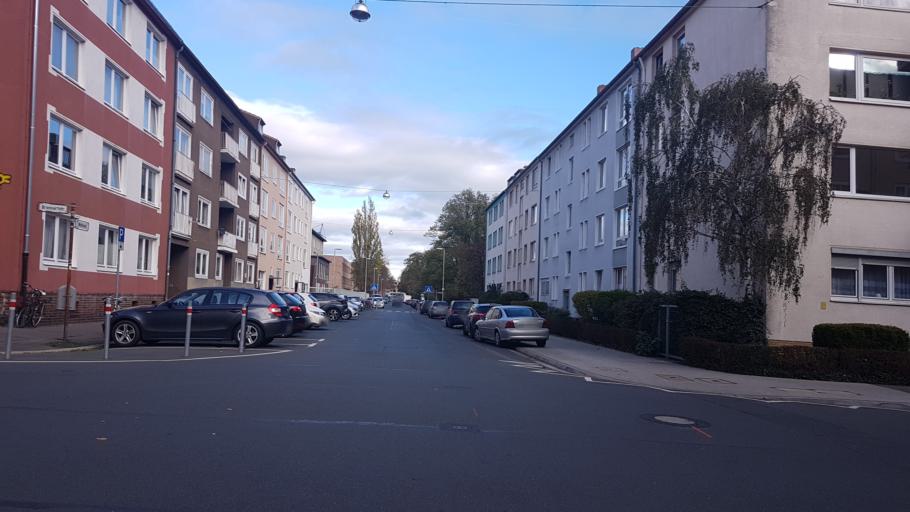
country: DE
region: Lower Saxony
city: Hannover
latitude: 52.3845
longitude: 9.7371
